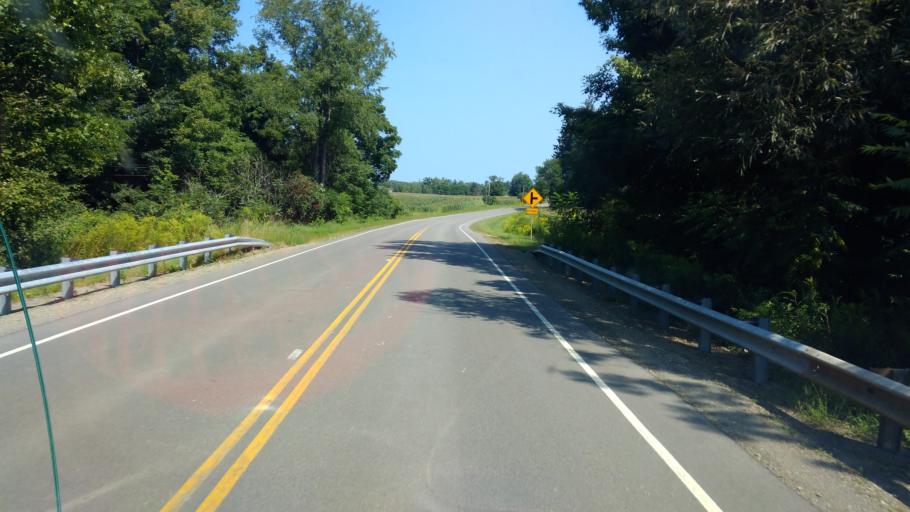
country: US
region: New York
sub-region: Allegany County
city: Belmont
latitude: 42.2643
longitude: -78.0520
